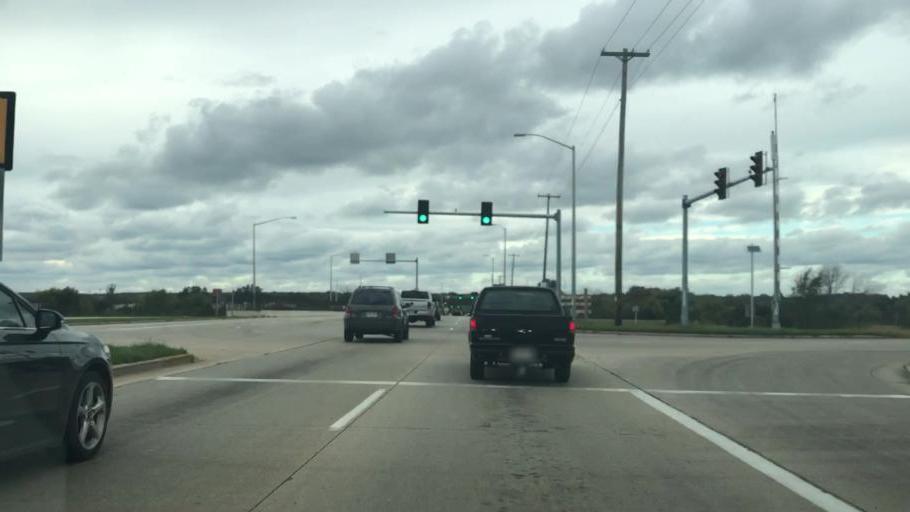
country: US
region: Wisconsin
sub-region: Waukesha County
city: Mukwonago
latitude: 42.8507
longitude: -88.3206
